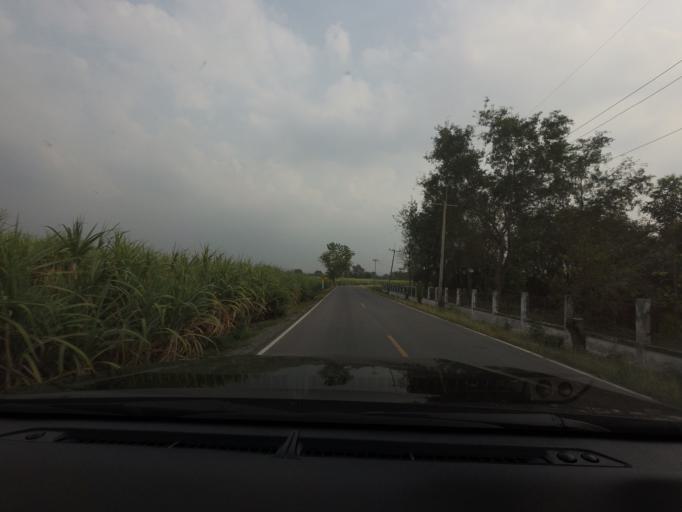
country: TH
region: Sara Buri
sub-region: Amphoe Wang Muang
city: Wang Muang
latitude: 14.8459
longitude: 101.1018
